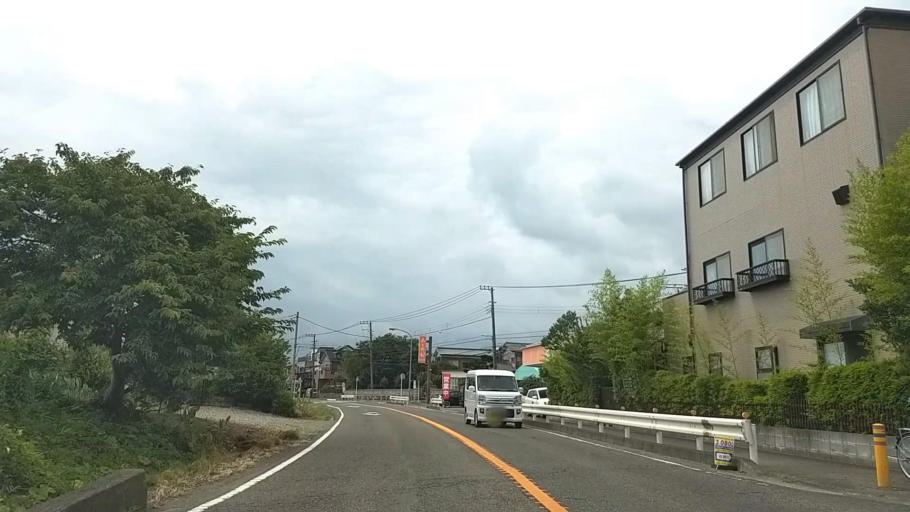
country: JP
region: Kanagawa
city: Chigasaki
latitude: 35.3690
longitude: 139.3995
